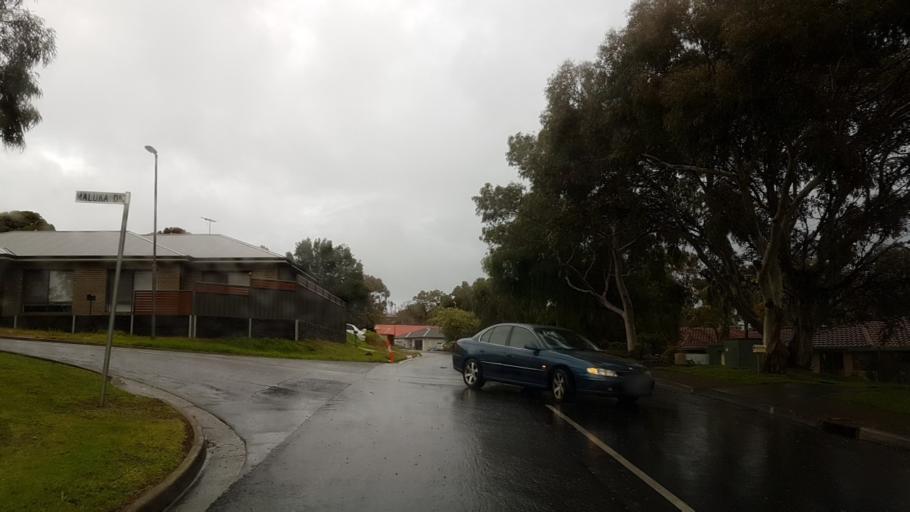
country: AU
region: South Australia
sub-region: Onkaparinga
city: Craigburn Farm
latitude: -35.0817
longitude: 138.5915
